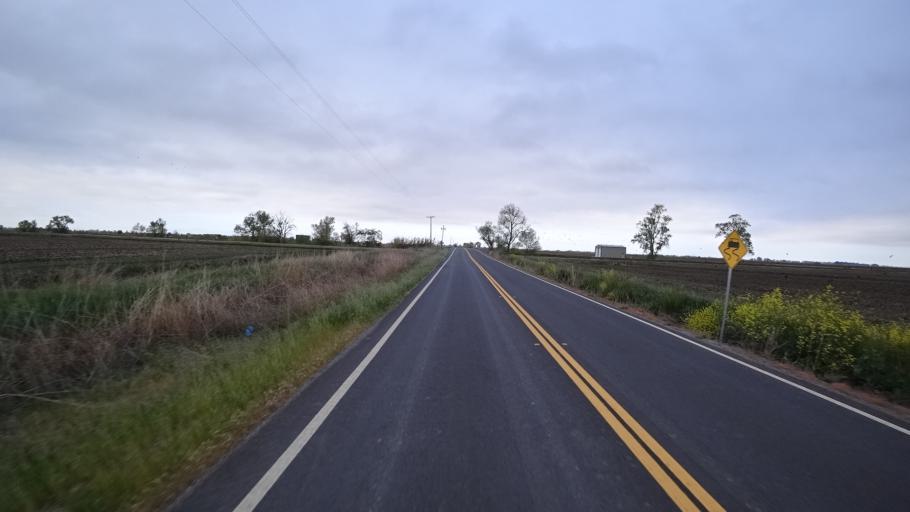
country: US
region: California
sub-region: Glenn County
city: Willows
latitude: 39.4064
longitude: -122.0792
